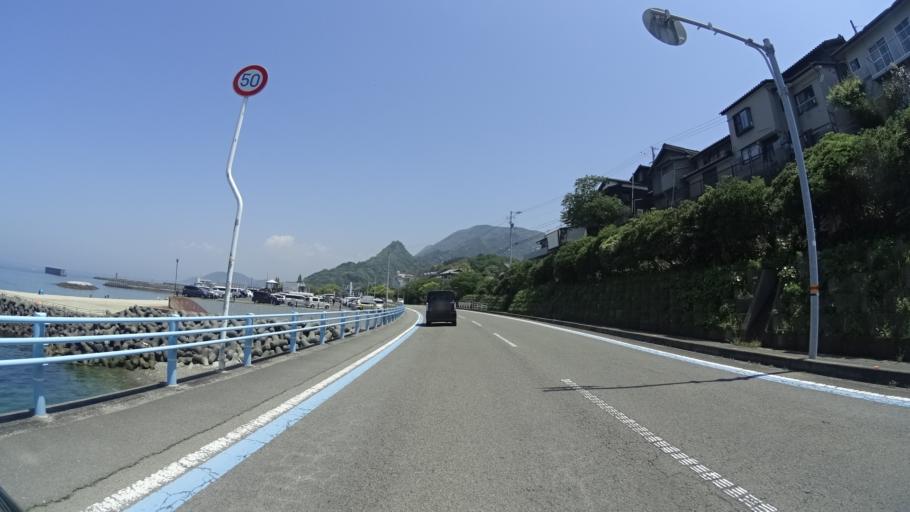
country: JP
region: Ehime
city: Iyo
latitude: 33.6845
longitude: 132.6324
